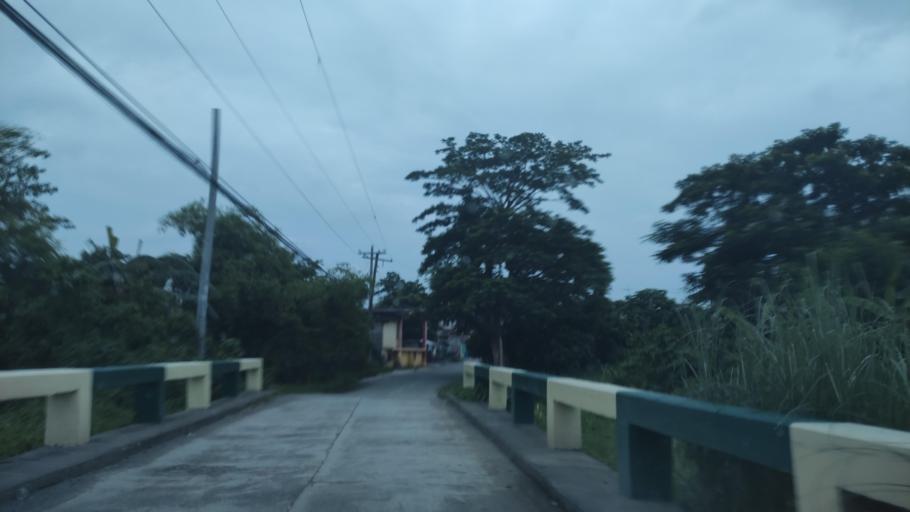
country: PH
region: Central Luzon
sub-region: Province of Nueva Ecija
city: San Anton
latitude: 15.3599
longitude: 120.9041
